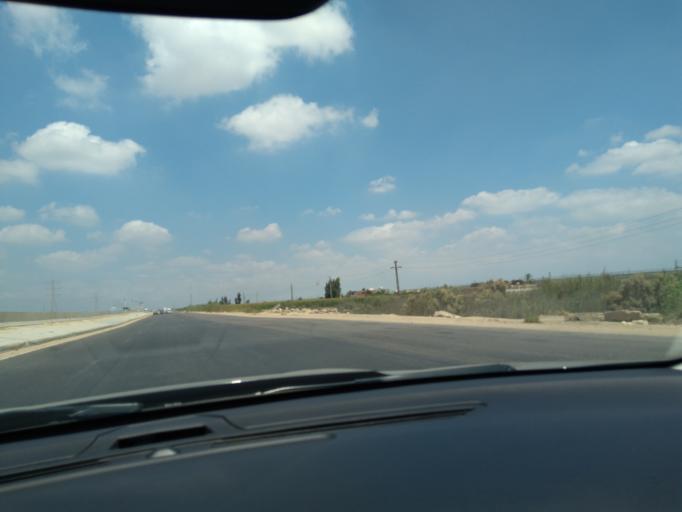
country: EG
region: Al Isma'iliyah
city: Ismailia
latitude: 30.9254
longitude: 32.3097
